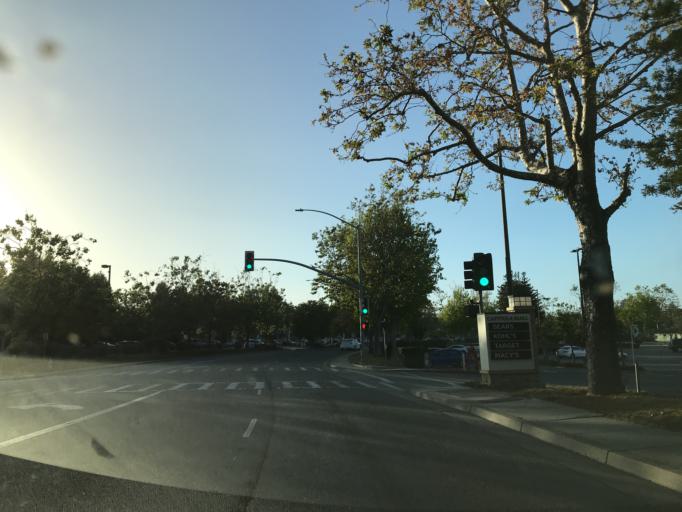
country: US
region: California
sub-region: Santa Cruz County
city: Live Oak
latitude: 36.9764
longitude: -121.9695
